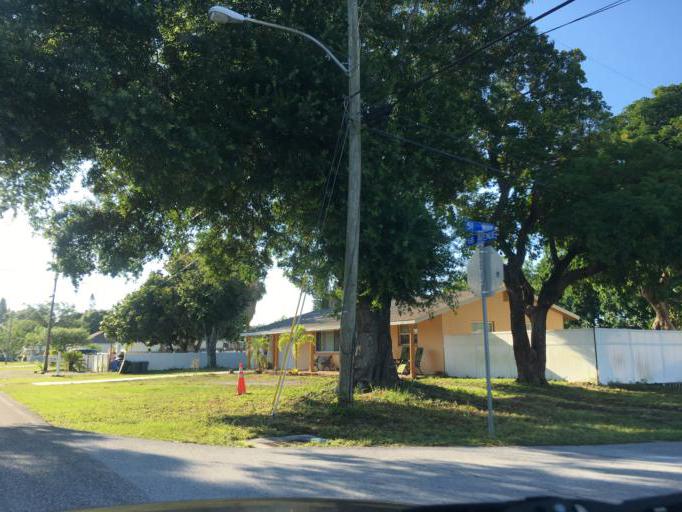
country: US
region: Florida
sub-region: Pinellas County
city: Pinellas Park
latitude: 27.8338
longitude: -82.7035
